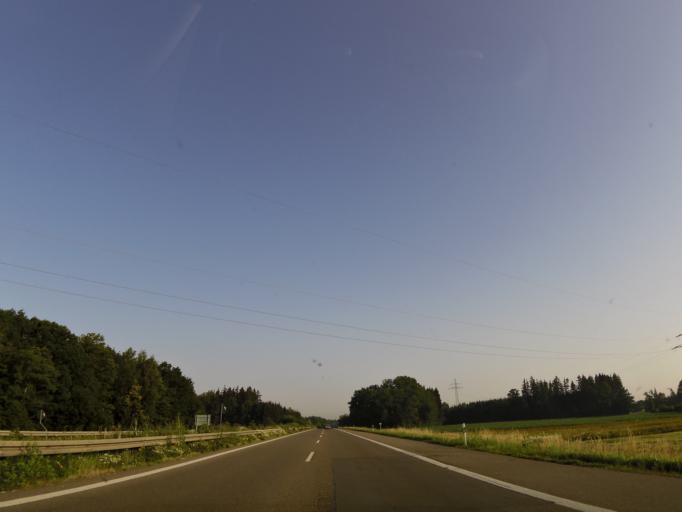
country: DE
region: Bavaria
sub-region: Swabia
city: Vohringen
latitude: 48.3045
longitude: 10.1035
